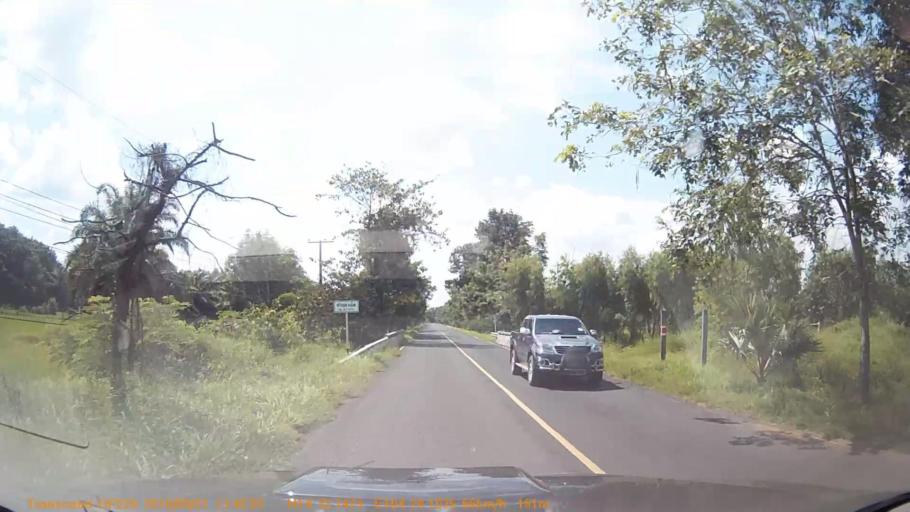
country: TH
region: Sisaket
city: Khun Han
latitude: 14.5460
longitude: 104.4678
